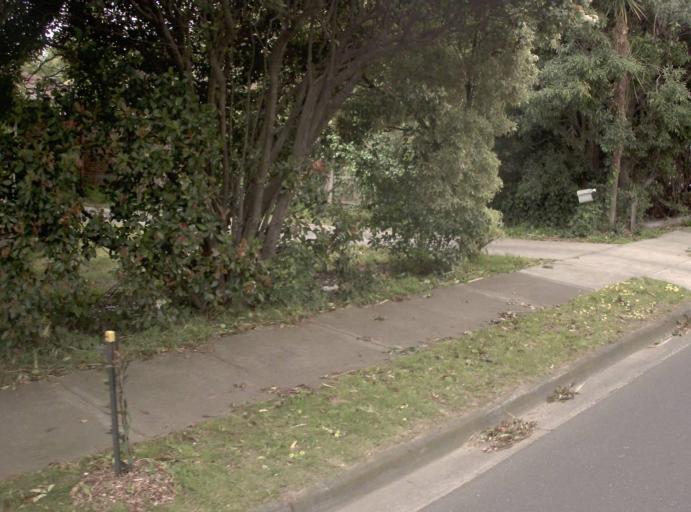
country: AU
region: Victoria
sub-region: Maroondah
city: Heathmont
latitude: -37.8275
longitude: 145.2272
